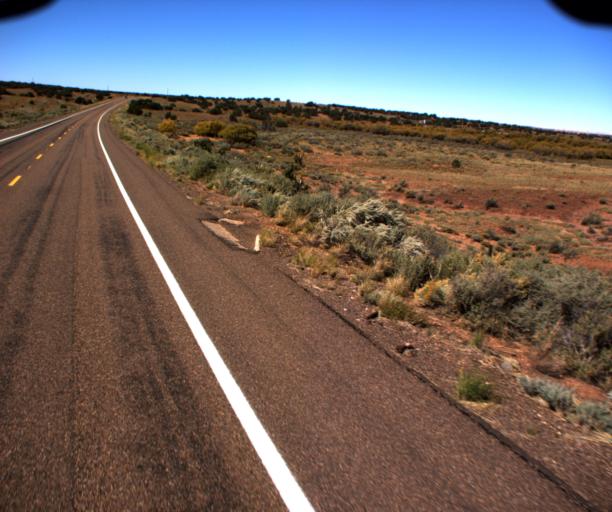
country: US
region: Arizona
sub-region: Apache County
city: Saint Johns
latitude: 34.5965
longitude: -109.6284
